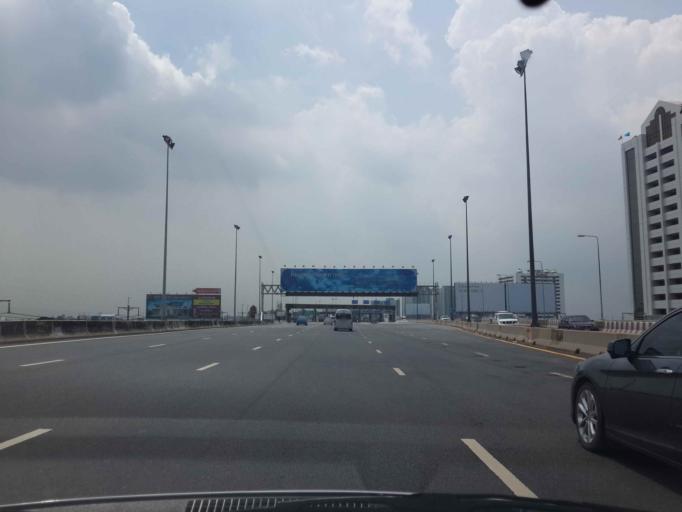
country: TH
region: Bangkok
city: Bang Na
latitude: 13.6611
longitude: 100.6617
